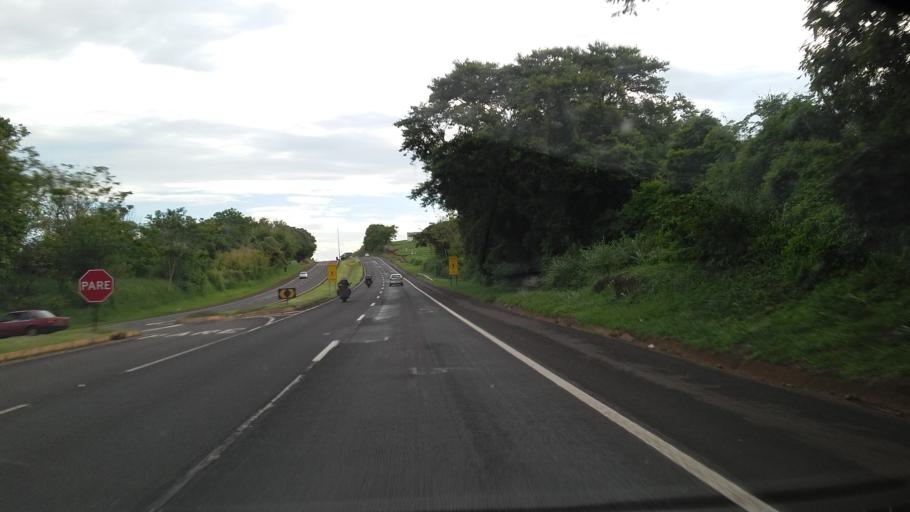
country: BR
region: Parana
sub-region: Paicandu
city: Paicandu
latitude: -23.5123
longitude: -52.0253
